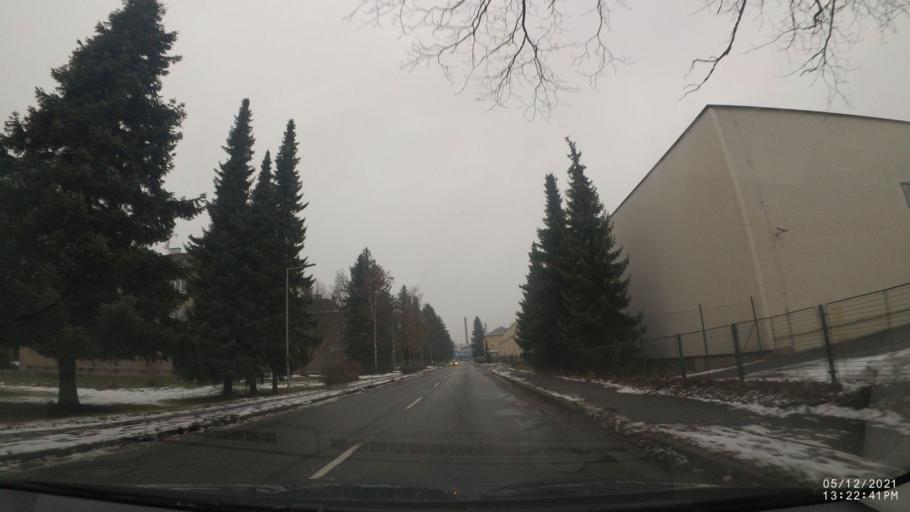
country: CZ
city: Velke Porici
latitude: 50.4663
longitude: 16.1824
